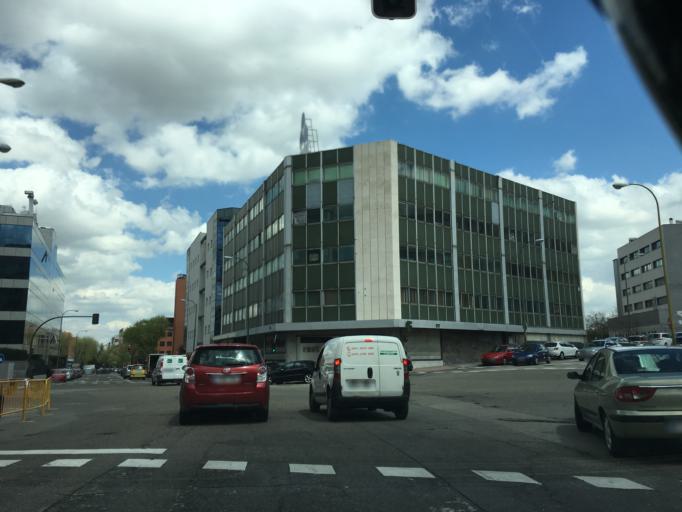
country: ES
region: Madrid
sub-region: Provincia de Madrid
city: San Blas
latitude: 40.4360
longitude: -3.6209
